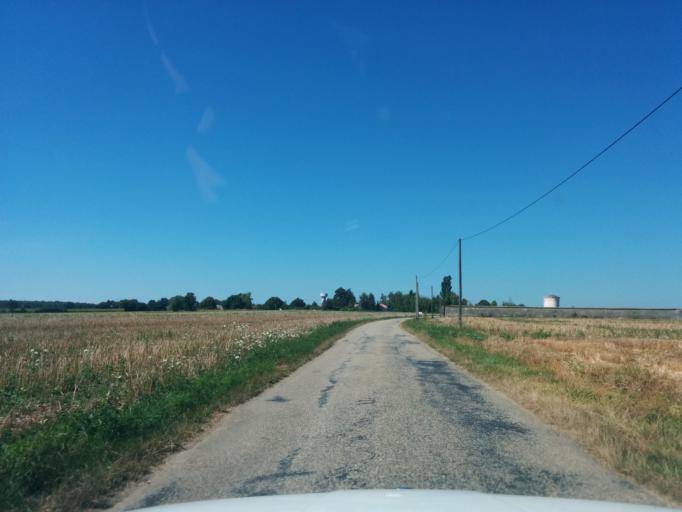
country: FR
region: Rhone-Alpes
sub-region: Departement de l'Ain
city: Perouges
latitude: 45.9266
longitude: 5.1523
